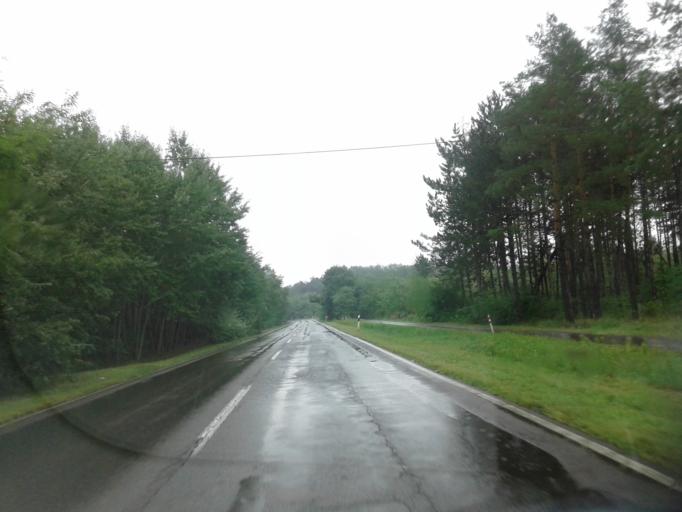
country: HU
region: Csongrad
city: Asotthalom
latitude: 46.2152
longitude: 19.8000
